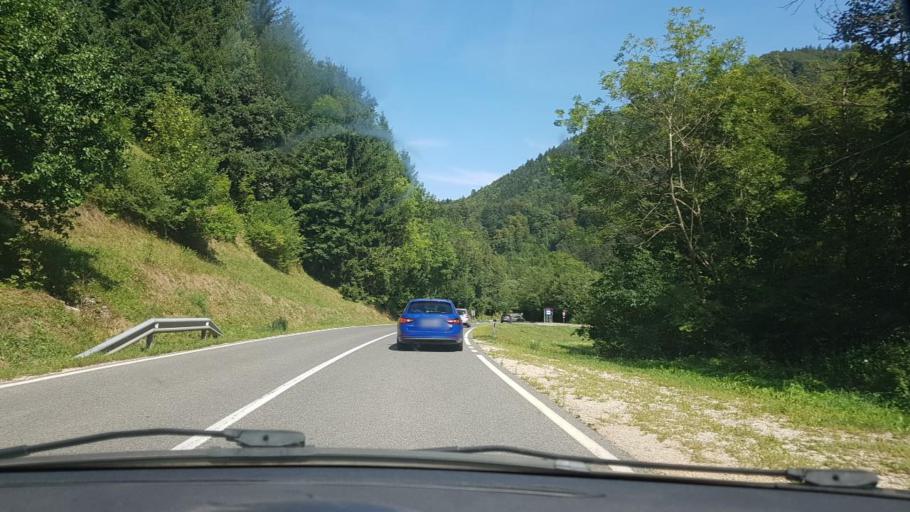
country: SI
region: Vransko
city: Vransko
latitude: 46.2197
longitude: 14.9369
